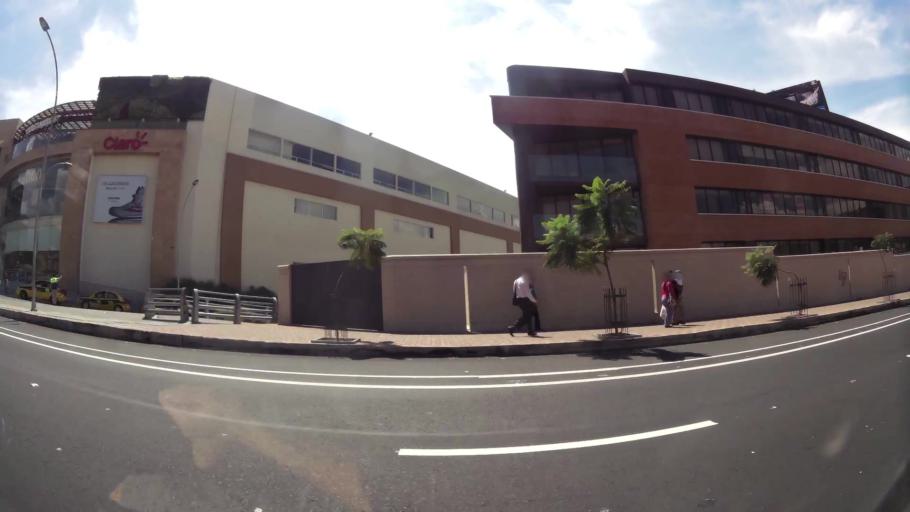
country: EC
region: Pichincha
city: Quito
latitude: -0.2082
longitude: -78.4257
